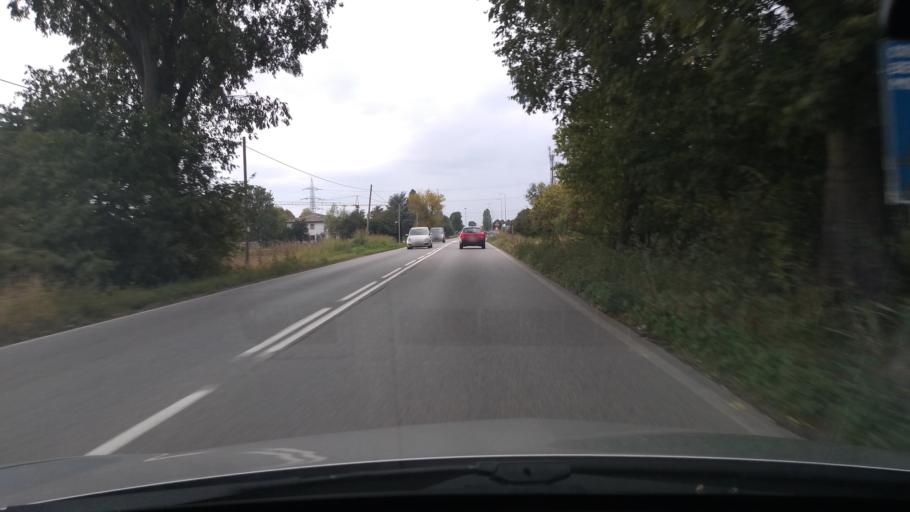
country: IT
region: Lombardy
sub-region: Provincia di Bergamo
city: Cologno al Serio
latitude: 45.5894
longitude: 9.7113
